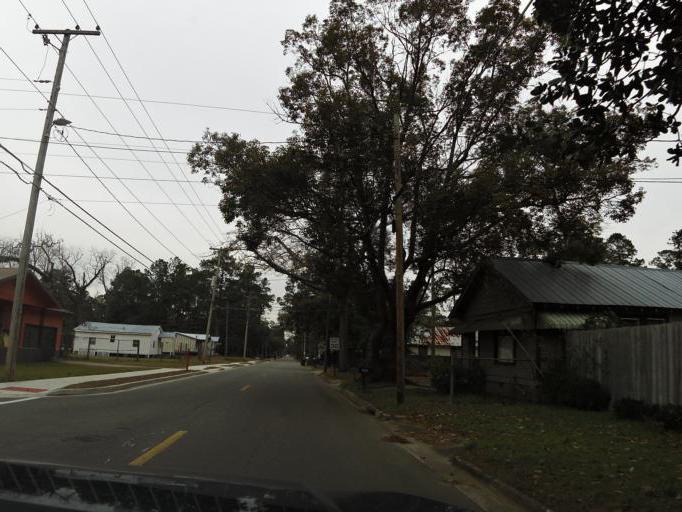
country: US
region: Georgia
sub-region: Thomas County
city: Thomasville
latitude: 30.8190
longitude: -83.9793
